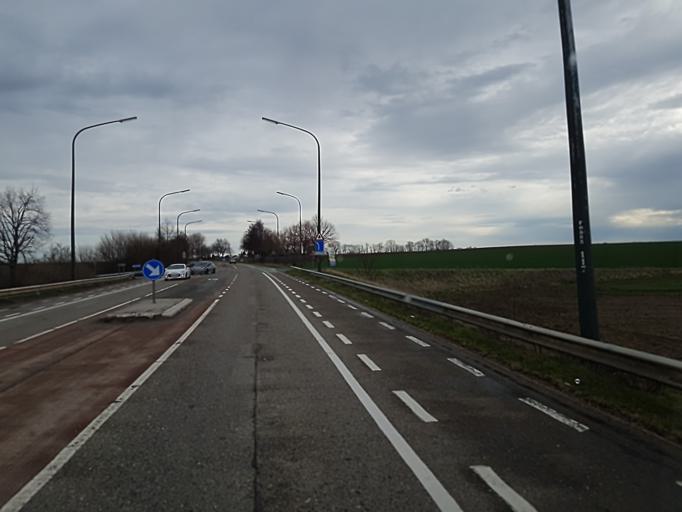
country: BE
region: Wallonia
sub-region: Province de Liege
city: Remicourt
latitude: 50.7086
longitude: 5.3039
